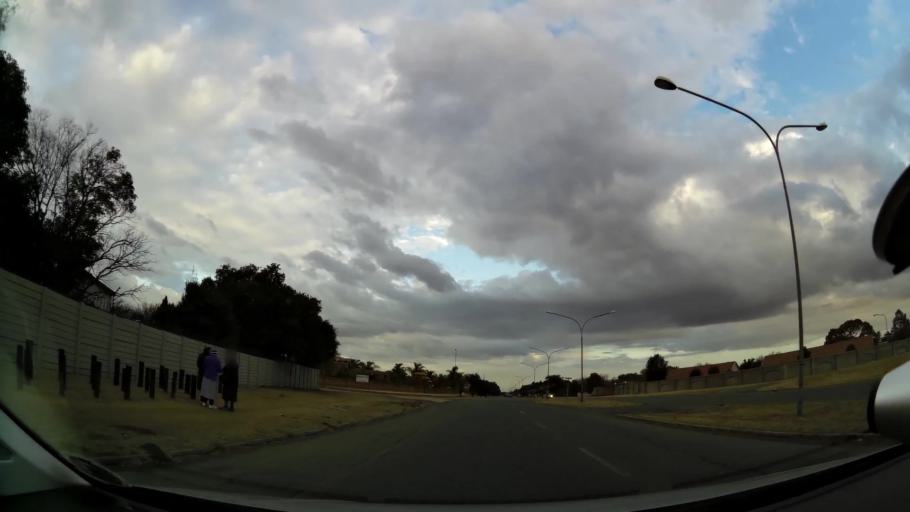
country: ZA
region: Orange Free State
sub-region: Lejweleputswa District Municipality
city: Welkom
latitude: -27.9566
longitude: 26.7359
